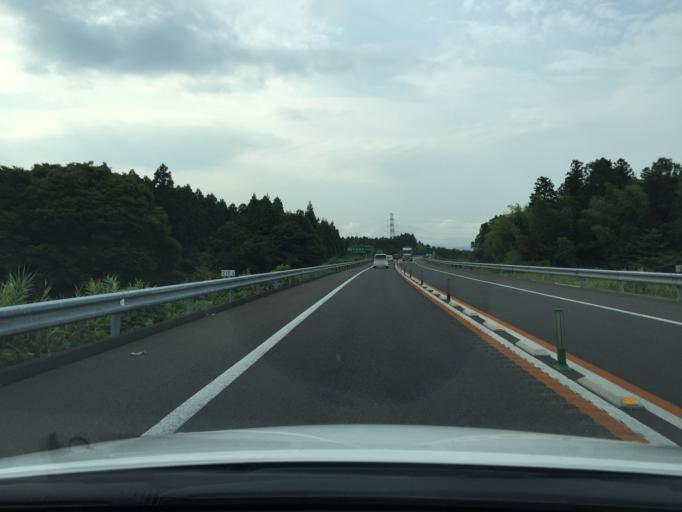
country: JP
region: Fukushima
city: Namie
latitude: 37.3562
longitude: 140.9746
